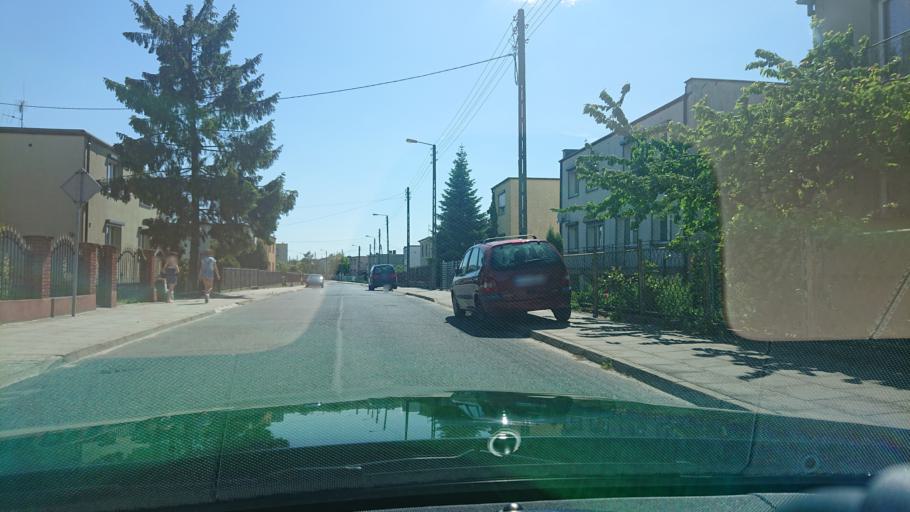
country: PL
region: Greater Poland Voivodeship
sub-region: Powiat gnieznienski
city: Gniezno
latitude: 52.5106
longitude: 17.5902
